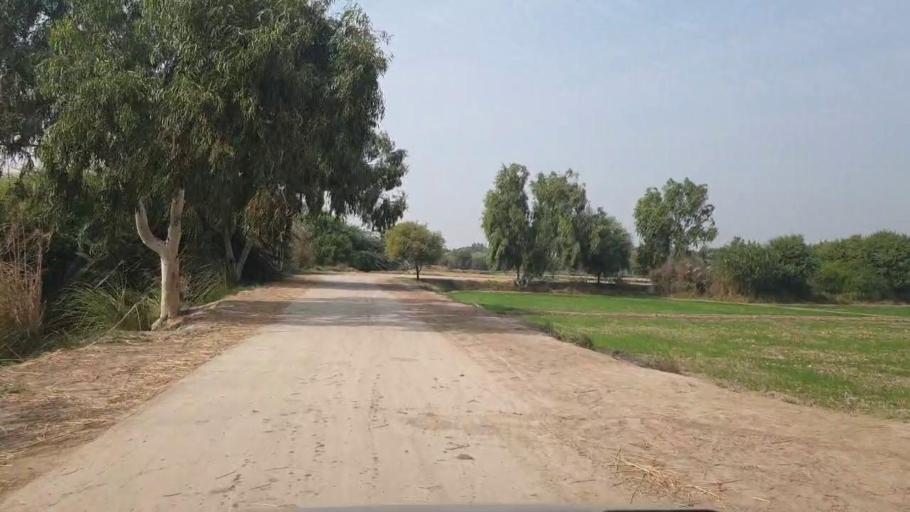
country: PK
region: Sindh
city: Tando Muhammad Khan
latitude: 25.1210
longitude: 68.4606
